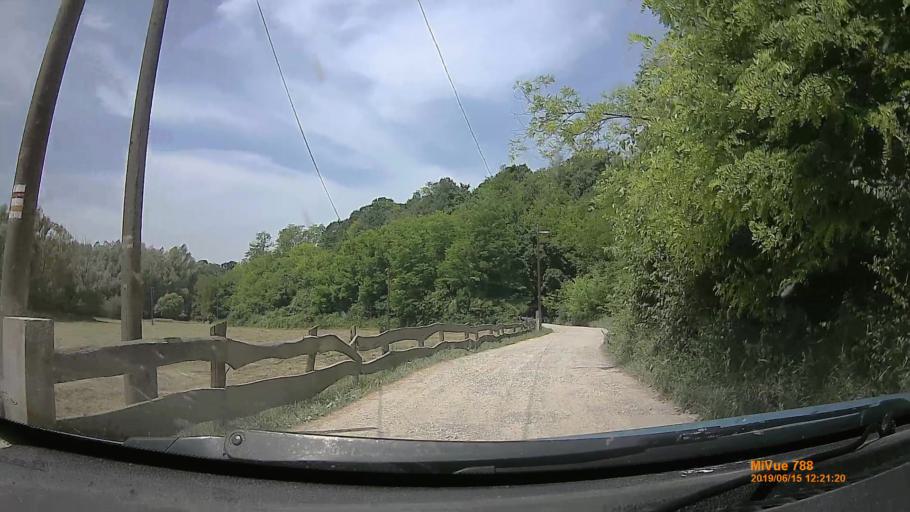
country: HU
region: Baranya
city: Buekkoesd
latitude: 46.1080
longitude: 18.0119
